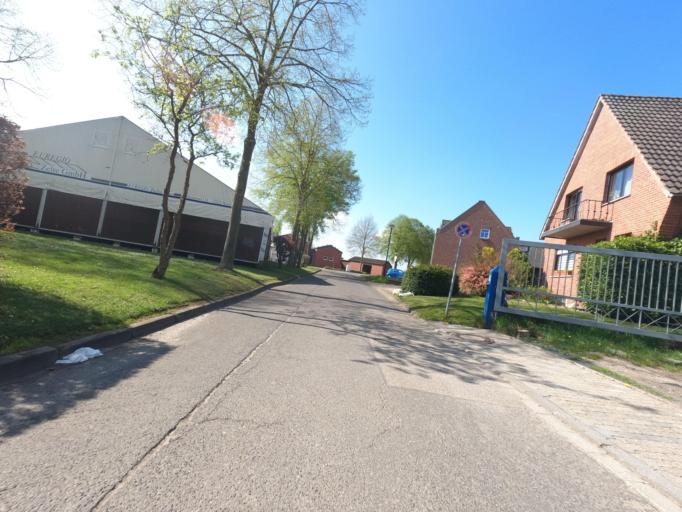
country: DE
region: North Rhine-Westphalia
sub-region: Regierungsbezirk Koln
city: Heinsberg
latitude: 51.0335
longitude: 6.0748
